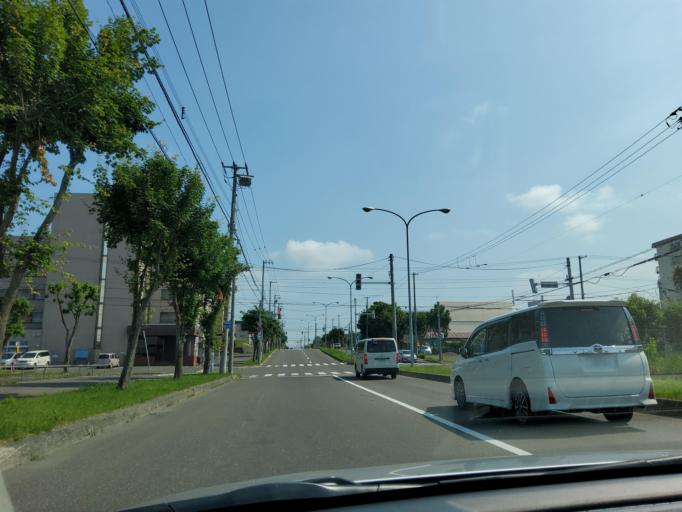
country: JP
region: Hokkaido
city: Obihiro
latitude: 42.9188
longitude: 143.1930
